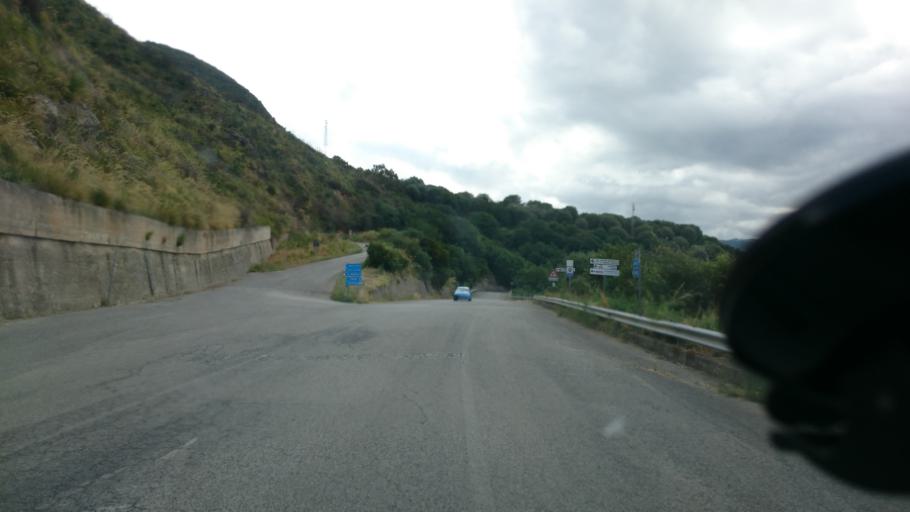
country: IT
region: Campania
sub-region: Provincia di Salerno
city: Pisciotta
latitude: 40.0907
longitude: 15.2535
